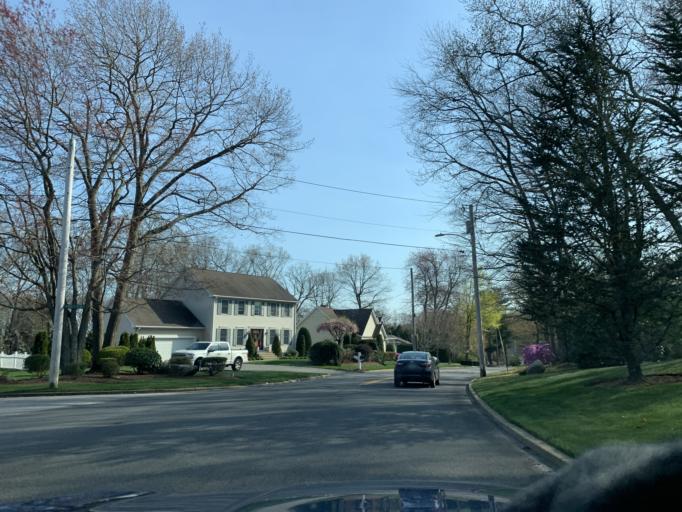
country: US
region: Rhode Island
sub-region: Providence County
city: Johnston
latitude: 41.7728
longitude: -71.5112
